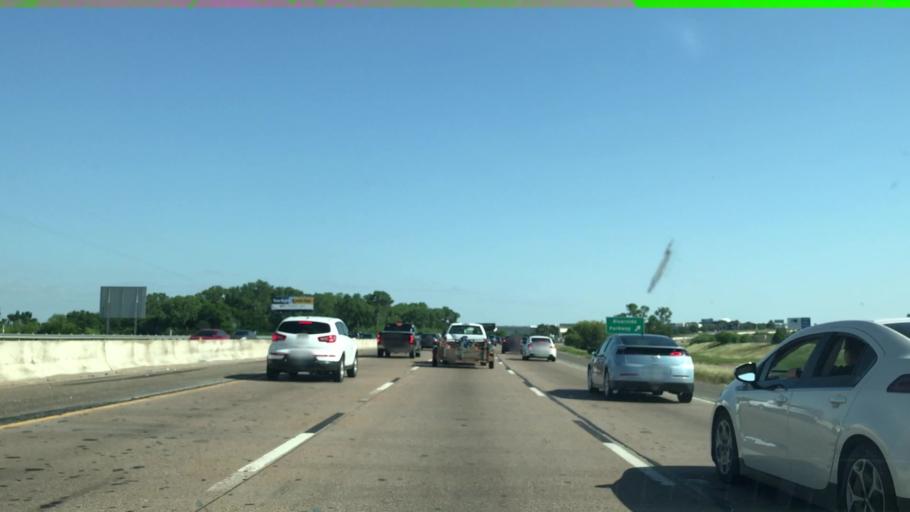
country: US
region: Texas
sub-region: Tarrant County
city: Euless
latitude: 32.8111
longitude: -97.0551
